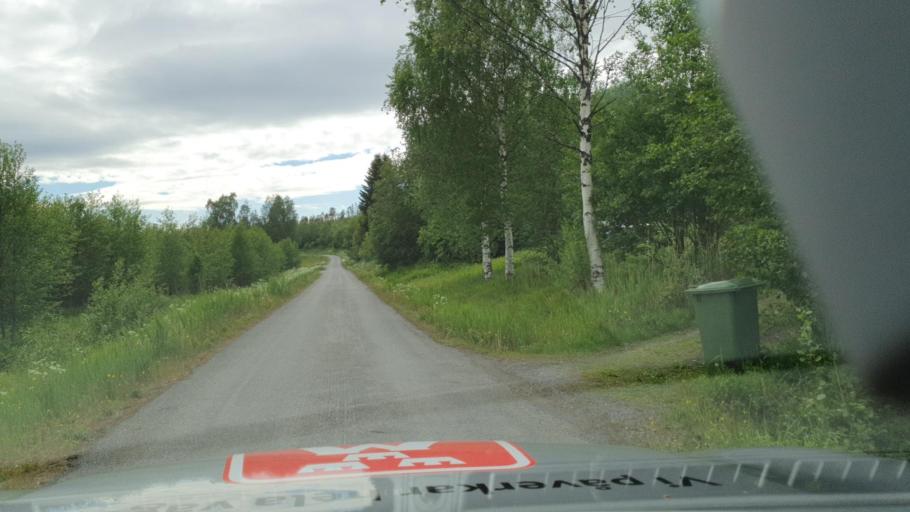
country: SE
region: Vaesternorrland
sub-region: Kramfors Kommun
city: Nordingra
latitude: 62.8495
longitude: 18.3433
